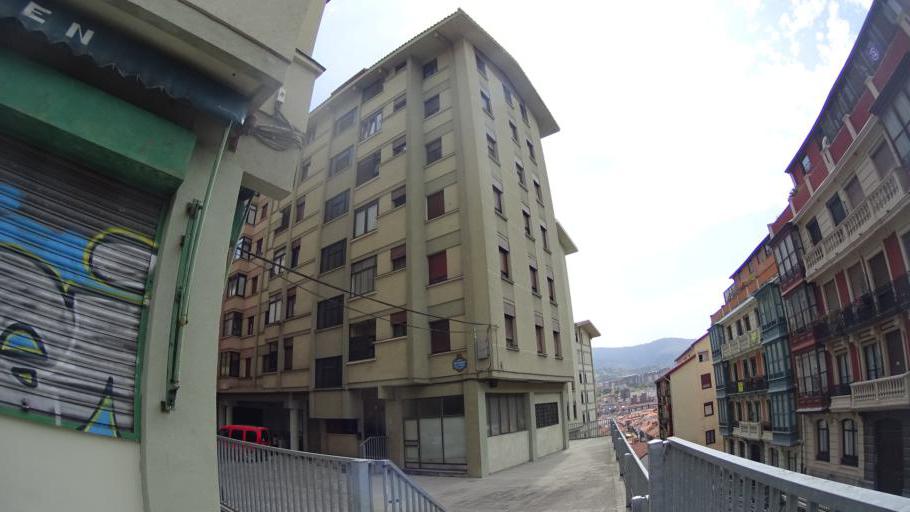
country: ES
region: Basque Country
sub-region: Bizkaia
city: Bilbao
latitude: 43.2595
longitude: -2.9206
